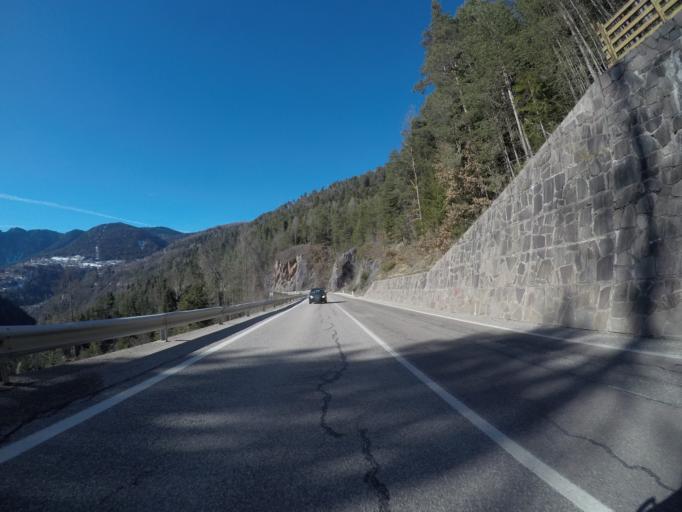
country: IT
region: Trentino-Alto Adige
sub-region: Bolzano
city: Anterivo
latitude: 46.2662
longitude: 11.3694
